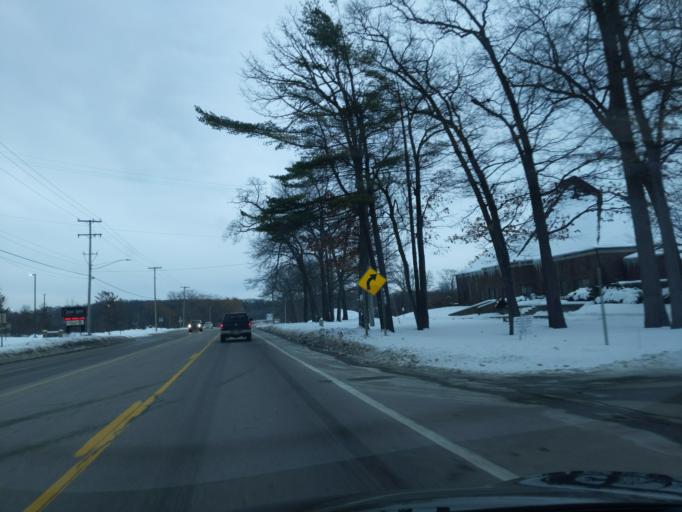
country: US
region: Michigan
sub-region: Ottawa County
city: Spring Lake
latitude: 43.0767
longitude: -86.1745
